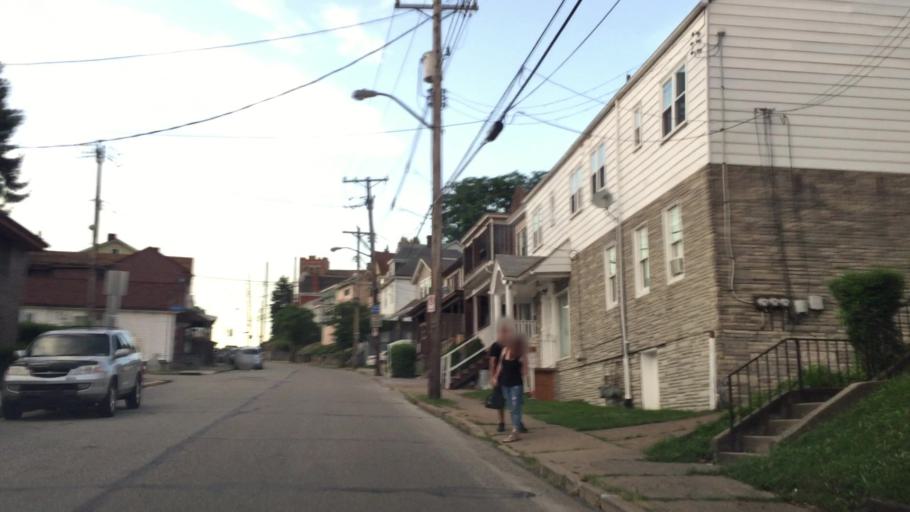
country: US
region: Pennsylvania
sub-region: Allegheny County
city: Pittsburgh
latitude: 40.4262
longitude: -80.0092
